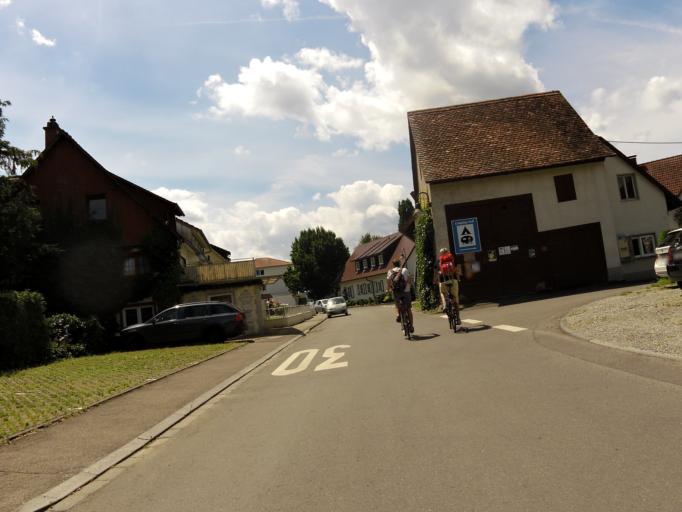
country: DE
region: Baden-Wuerttemberg
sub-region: Tuebingen Region
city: Uberlingen
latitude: 47.7521
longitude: 9.1934
